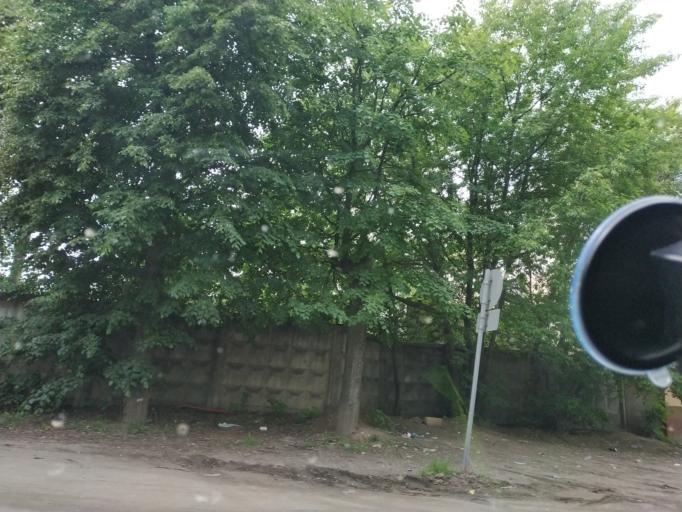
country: RU
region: Moskovskaya
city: Zhukovskiy
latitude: 55.5565
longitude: 38.1157
